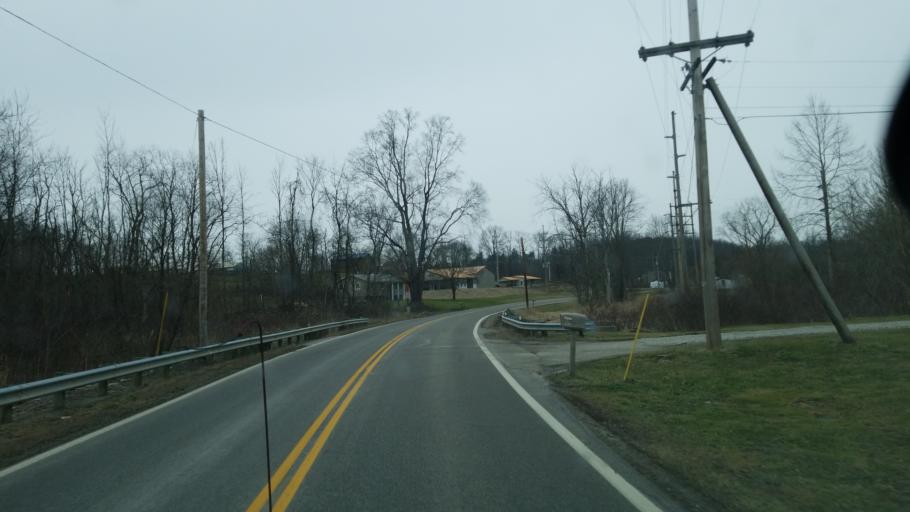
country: US
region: Ohio
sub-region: Guernsey County
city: Byesville
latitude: 40.0109
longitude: -81.5188
